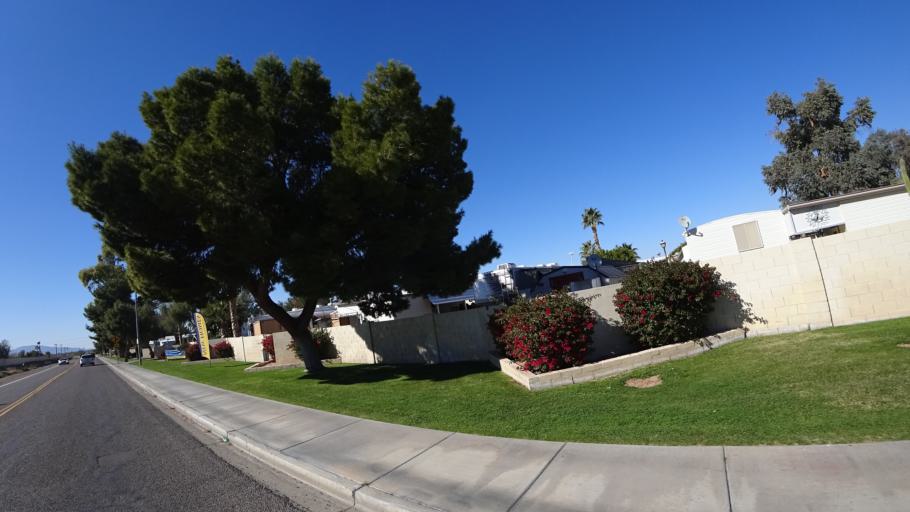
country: US
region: Arizona
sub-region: Maricopa County
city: Surprise
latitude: 33.6526
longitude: -112.2929
